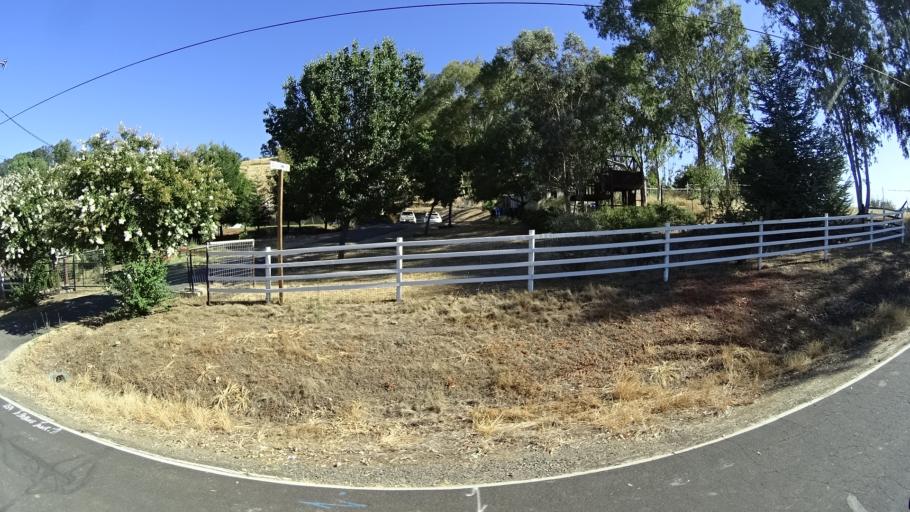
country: US
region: California
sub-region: Calaveras County
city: Rancho Calaveras
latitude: 38.1116
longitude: -120.8687
